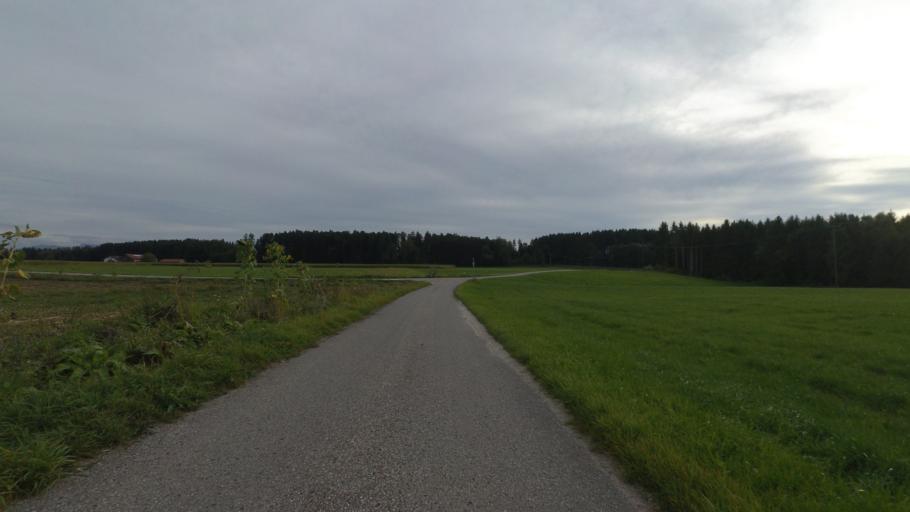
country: DE
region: Bavaria
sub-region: Upper Bavaria
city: Chieming
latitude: 47.9253
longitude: 12.5355
